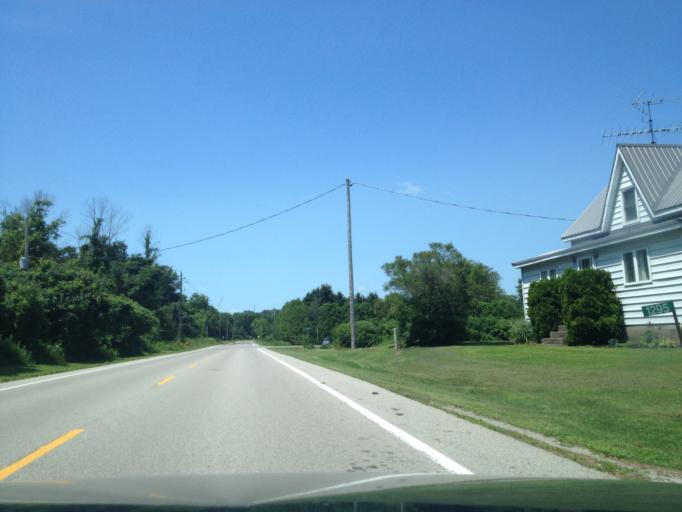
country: CA
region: Ontario
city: Norfolk County
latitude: 42.5847
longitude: -80.6123
